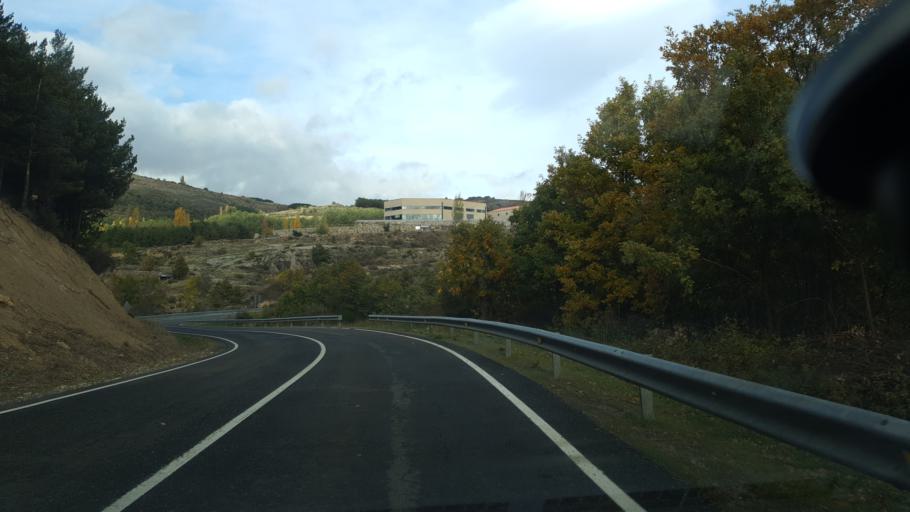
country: ES
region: Castille and Leon
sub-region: Provincia de Avila
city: Hoyocasero
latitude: 40.3994
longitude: -4.9858
